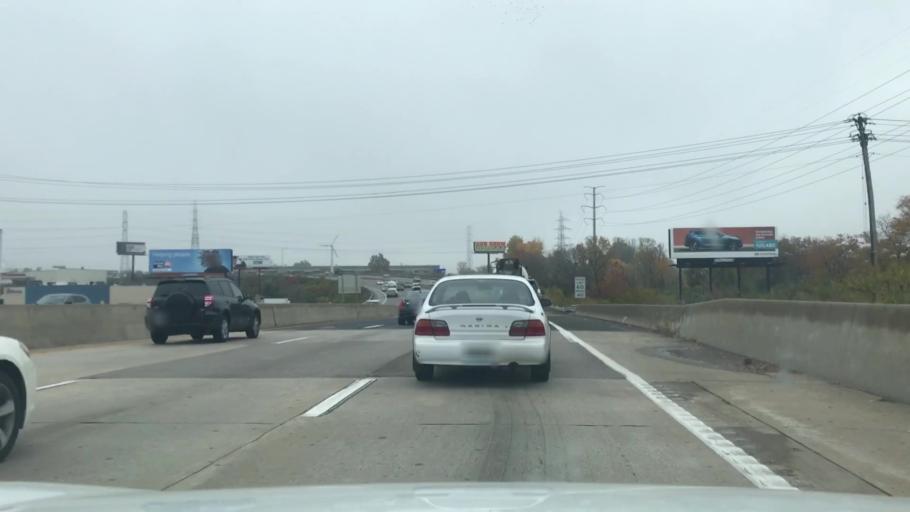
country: US
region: Missouri
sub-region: Saint Louis County
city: Vinita Park
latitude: 38.6807
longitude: -90.3575
